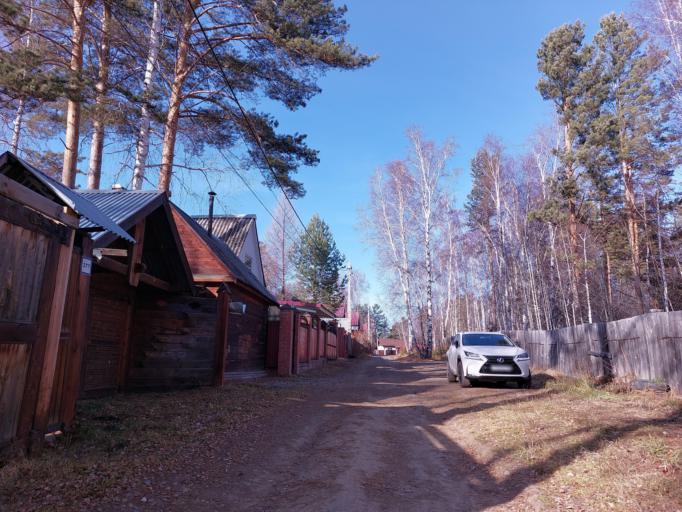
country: RU
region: Irkutsk
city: Pivovarikha
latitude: 52.1866
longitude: 104.4552
